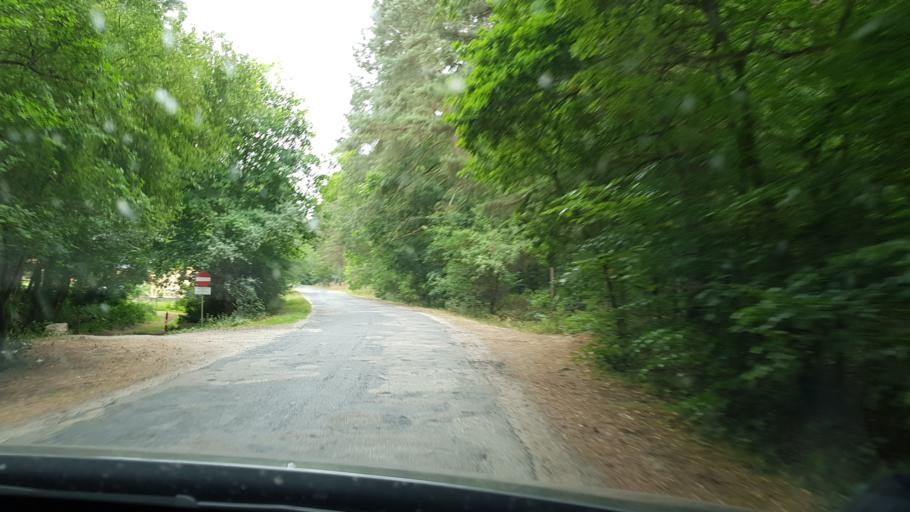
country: PL
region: West Pomeranian Voivodeship
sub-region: Powiat kamienski
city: Miedzyzdroje
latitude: 53.9571
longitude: 14.5683
